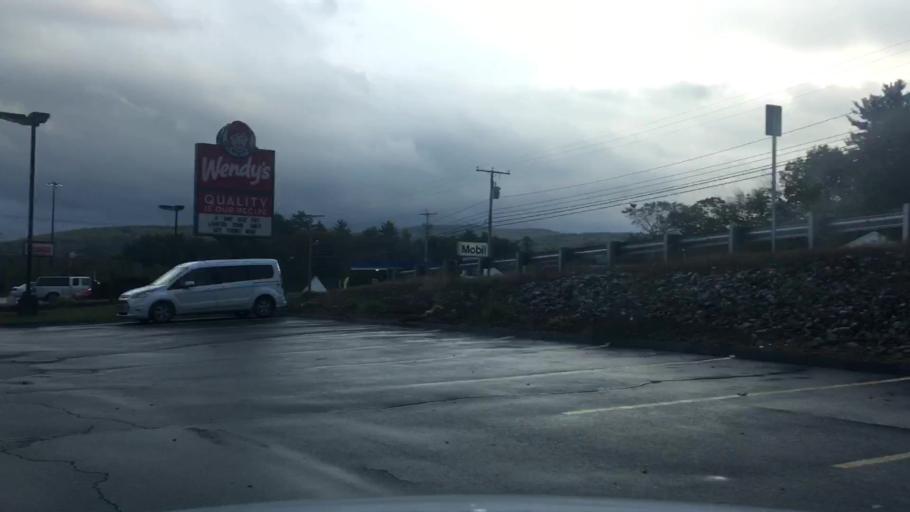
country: US
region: New Hampshire
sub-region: Merrimack County
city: Epsom
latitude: 43.2288
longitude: -71.3630
